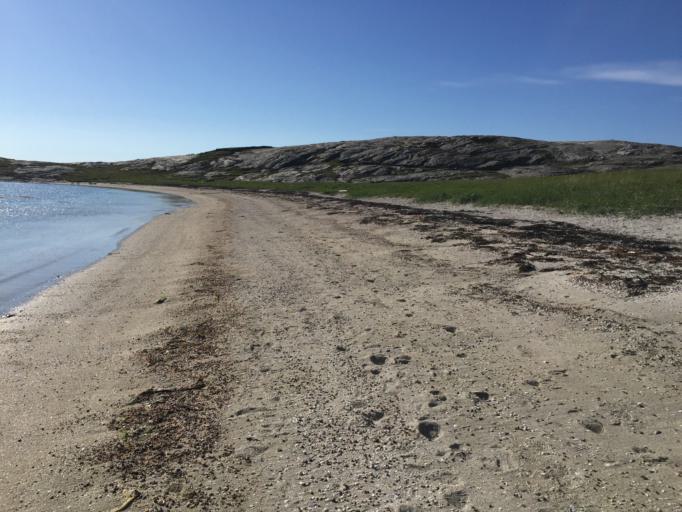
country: NO
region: Nordland
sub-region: Bodo
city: Loding
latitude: 67.4191
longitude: 14.6314
